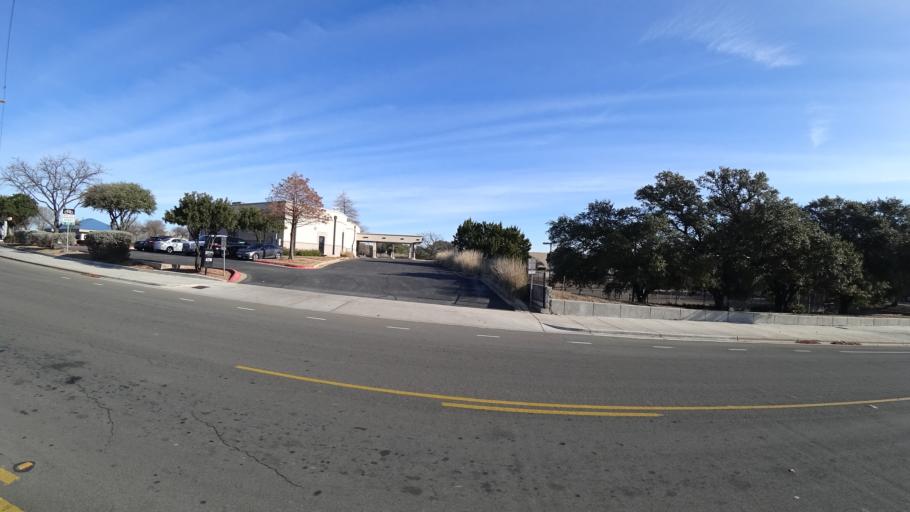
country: US
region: Texas
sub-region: Travis County
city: Wells Branch
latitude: 30.3902
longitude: -97.7136
